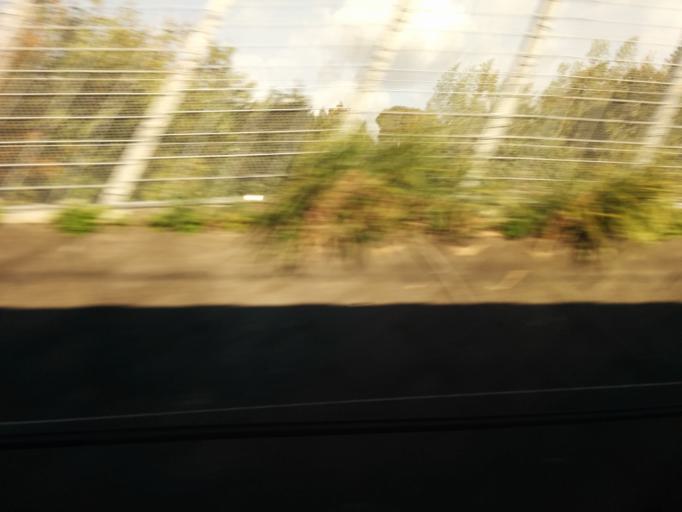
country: JP
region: Shizuoka
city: Shimada
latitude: 34.8074
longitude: 138.2118
